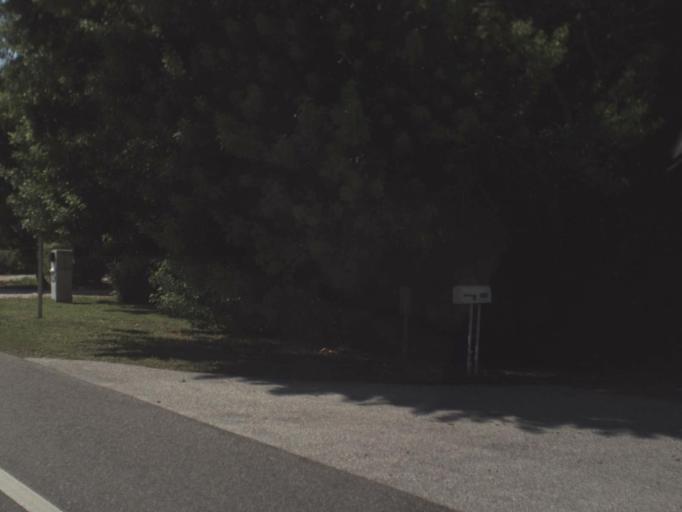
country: US
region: Florida
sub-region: Manatee County
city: Longboat Key
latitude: 27.4176
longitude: -82.6641
